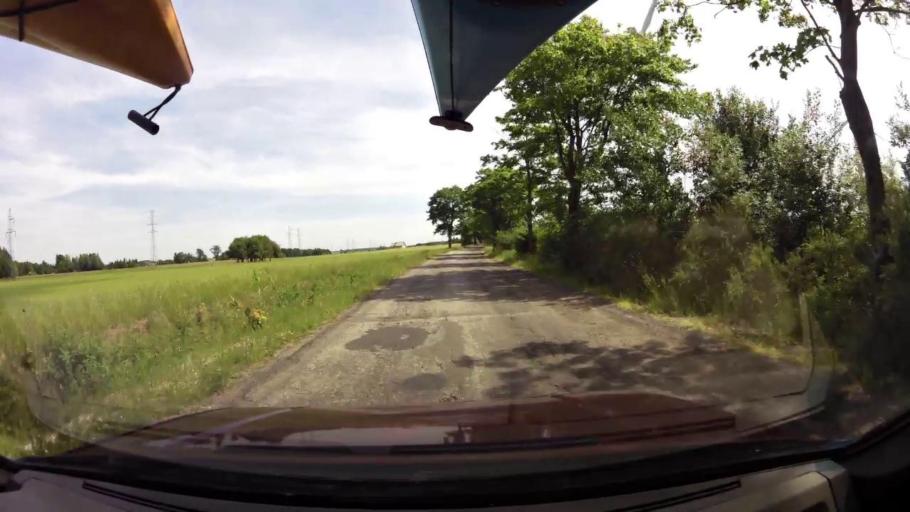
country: PL
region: West Pomeranian Voivodeship
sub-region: Powiat koszalinski
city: Sianow
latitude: 54.3213
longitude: 16.3371
